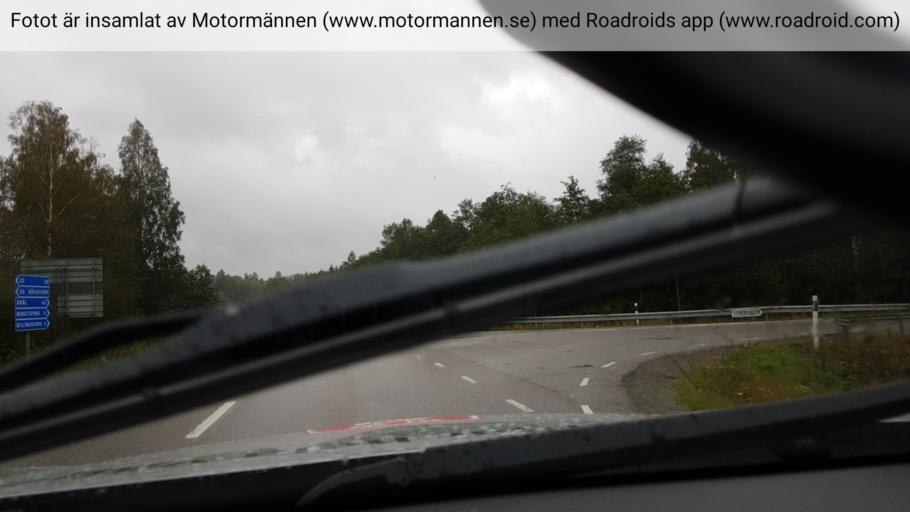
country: SE
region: Vaestra Goetaland
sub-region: Bengtsfors Kommun
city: Billingsfors
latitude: 58.9552
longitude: 12.2292
